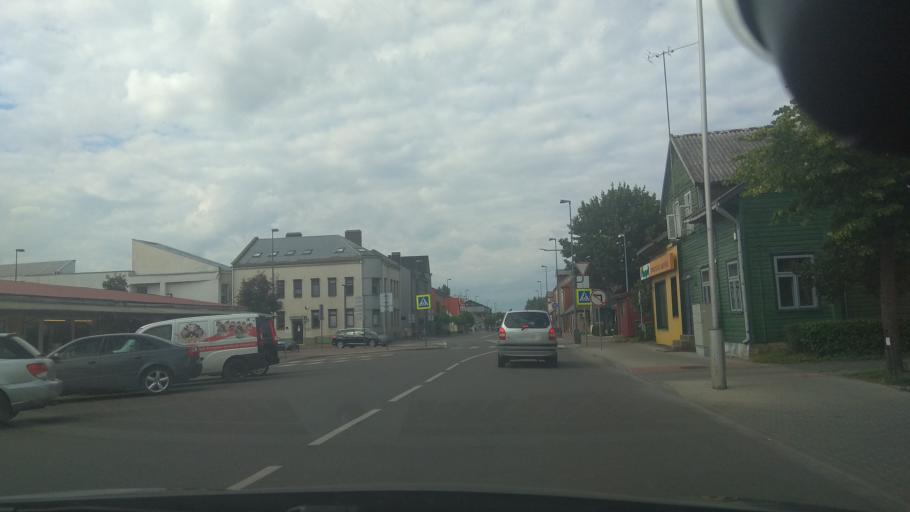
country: LT
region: Marijampoles apskritis
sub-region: Marijampole Municipality
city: Marijampole
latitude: 54.5541
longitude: 23.3540
